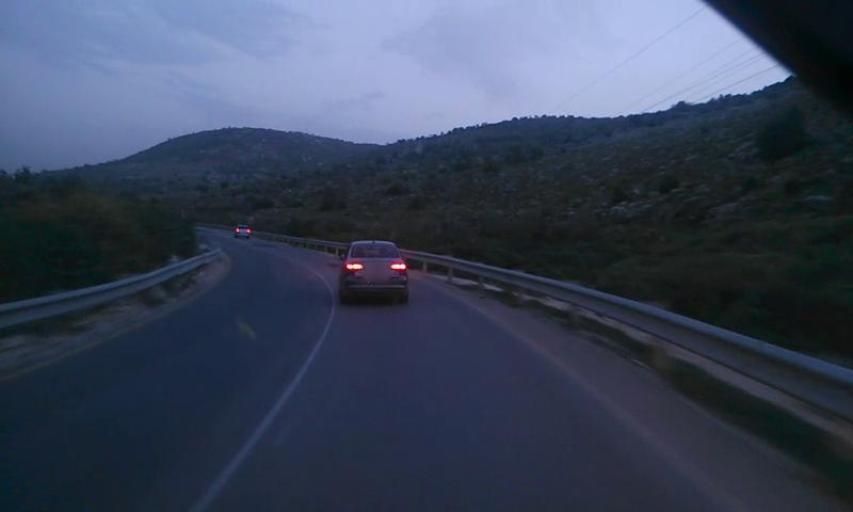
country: PS
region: West Bank
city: Ramin
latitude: 32.2860
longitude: 35.1366
